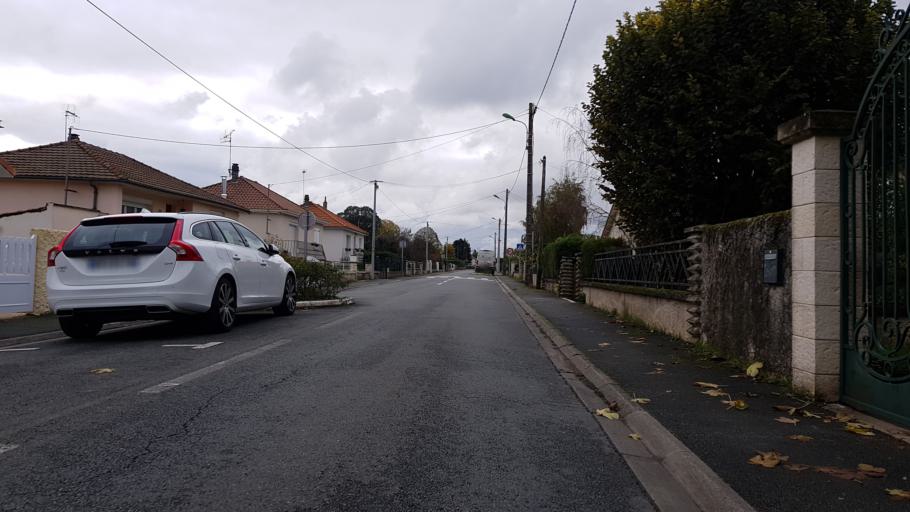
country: FR
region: Poitou-Charentes
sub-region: Departement de la Vienne
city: Chasseneuil-du-Poitou
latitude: 46.6453
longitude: 0.3668
